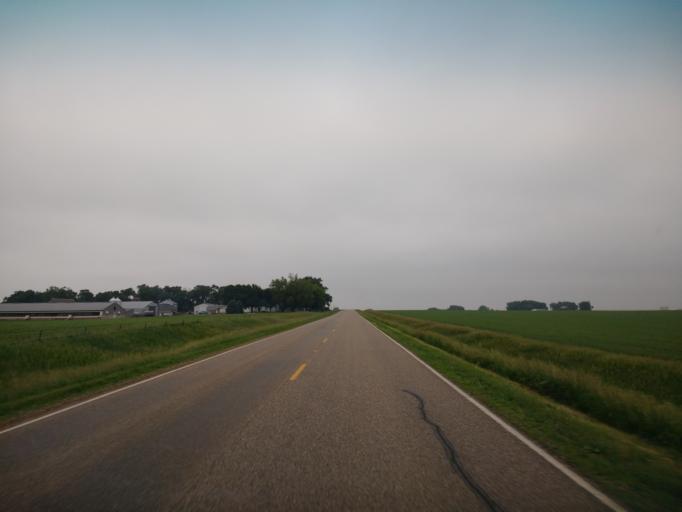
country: US
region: Iowa
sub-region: Sioux County
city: Alton
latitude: 42.9890
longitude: -95.8993
